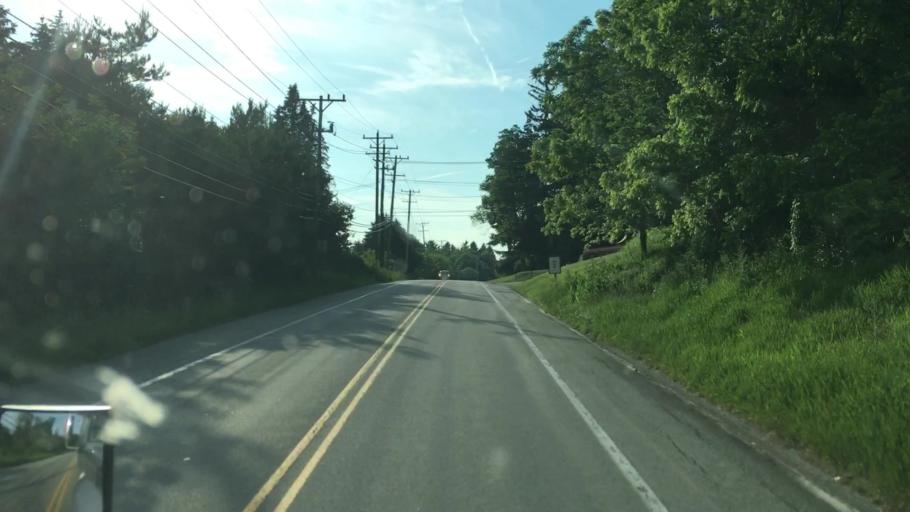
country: US
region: Pennsylvania
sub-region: Fayette County
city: Hopwood
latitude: 39.8011
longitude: -79.5523
